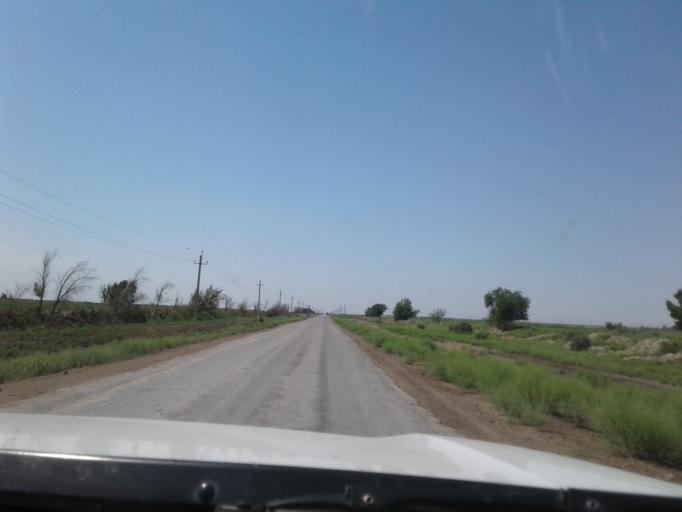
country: TM
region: Dasoguz
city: Koeneuergench
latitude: 41.8484
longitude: 58.7048
